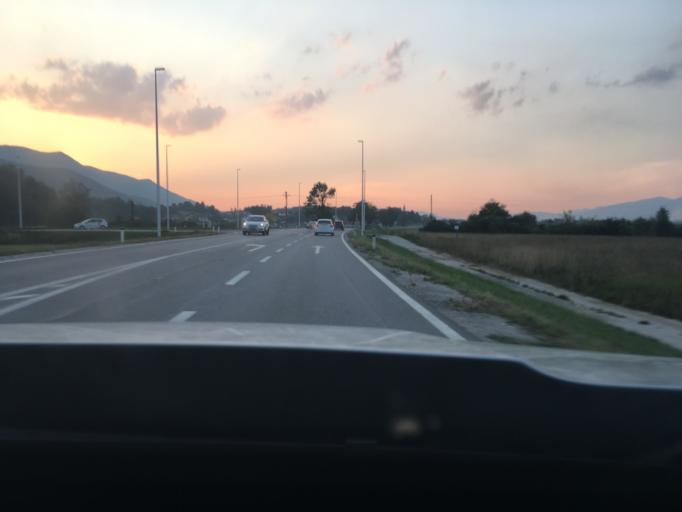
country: SI
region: Ribnica
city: Ribnica
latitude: 45.6978
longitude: 14.7634
